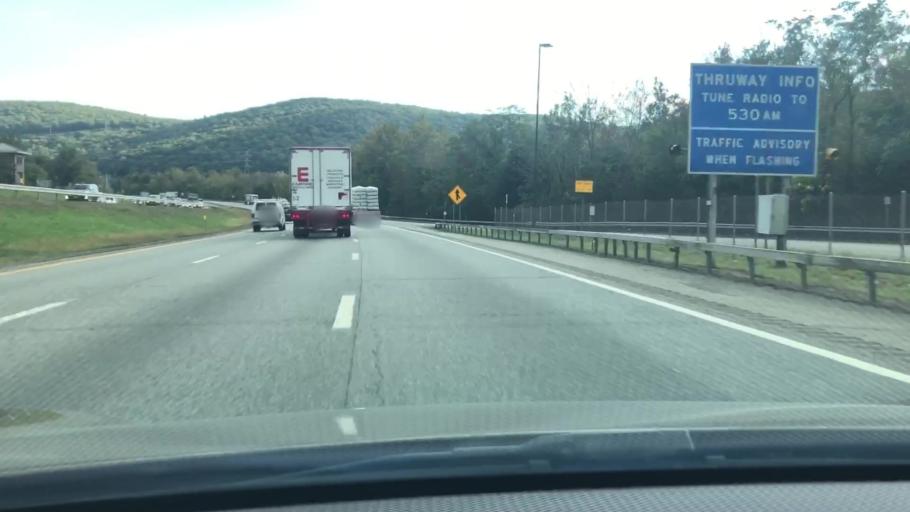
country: US
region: New York
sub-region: Rockland County
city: Sloatsburg
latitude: 41.1516
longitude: -74.1893
